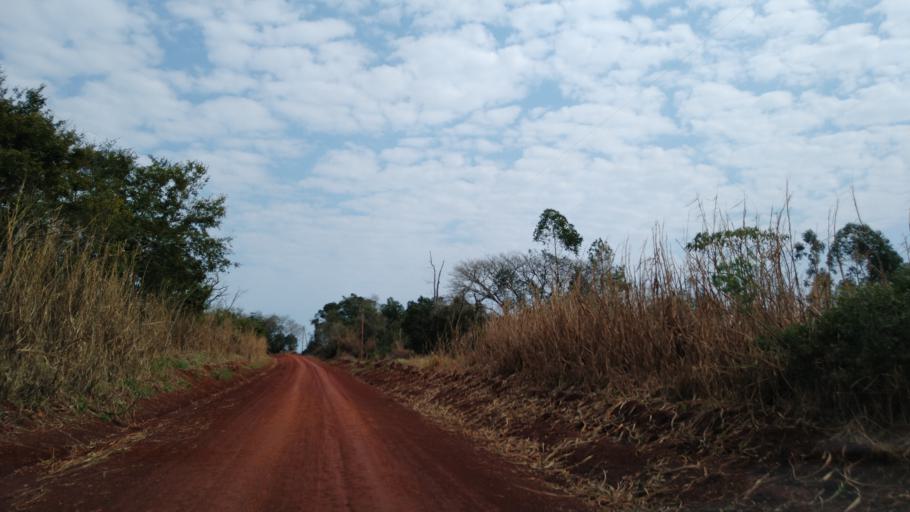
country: AR
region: Misiones
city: Capiovi
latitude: -26.9424
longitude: -55.0655
